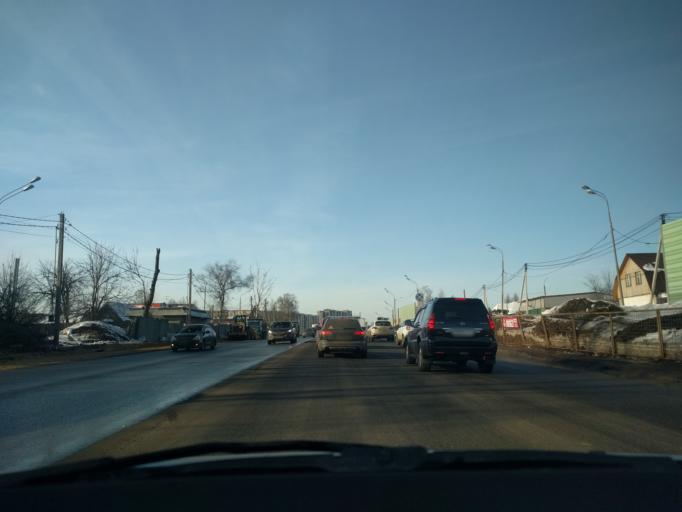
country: RU
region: Moscow
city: Severnyy
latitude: 55.9540
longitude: 37.5367
